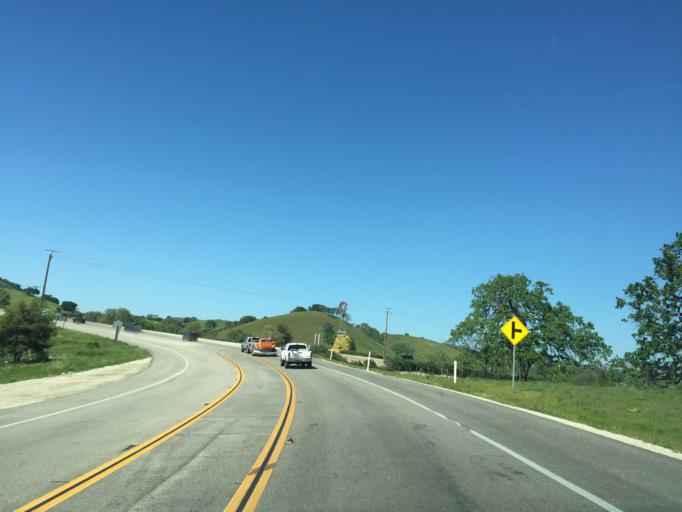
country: US
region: California
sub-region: Santa Barbara County
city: Los Olivos
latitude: 34.6861
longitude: -120.1551
